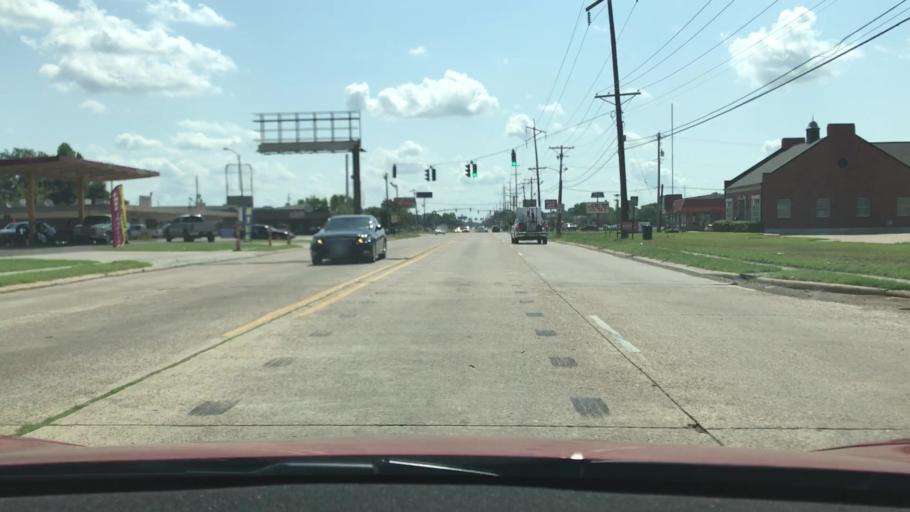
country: US
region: Louisiana
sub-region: Caddo Parish
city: Shreveport
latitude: 32.4420
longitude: -93.7864
